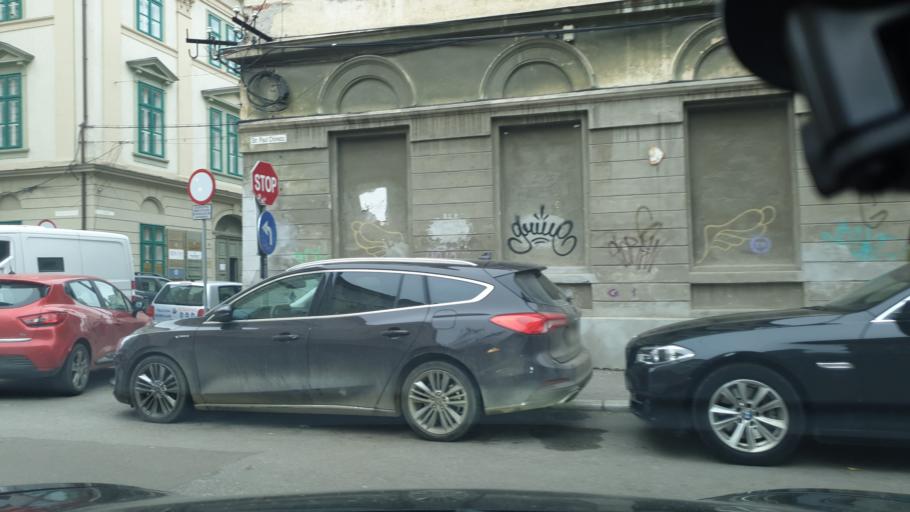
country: RO
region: Timis
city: Timisoara
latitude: 45.7575
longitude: 21.2308
